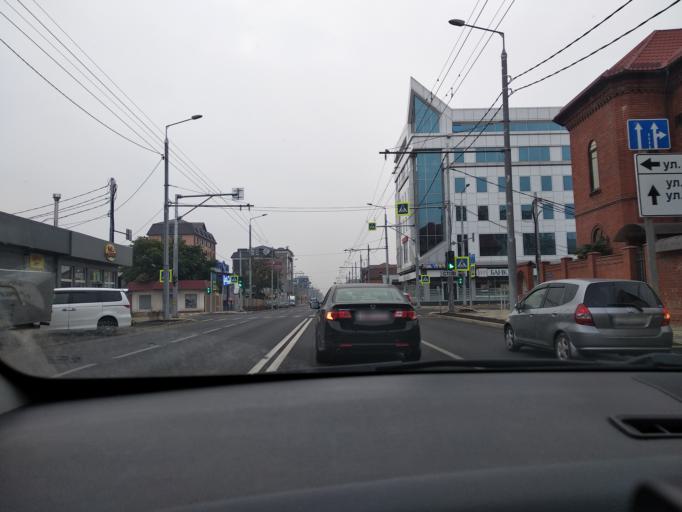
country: RU
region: Krasnodarskiy
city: Krasnodar
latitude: 45.0497
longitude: 38.9586
